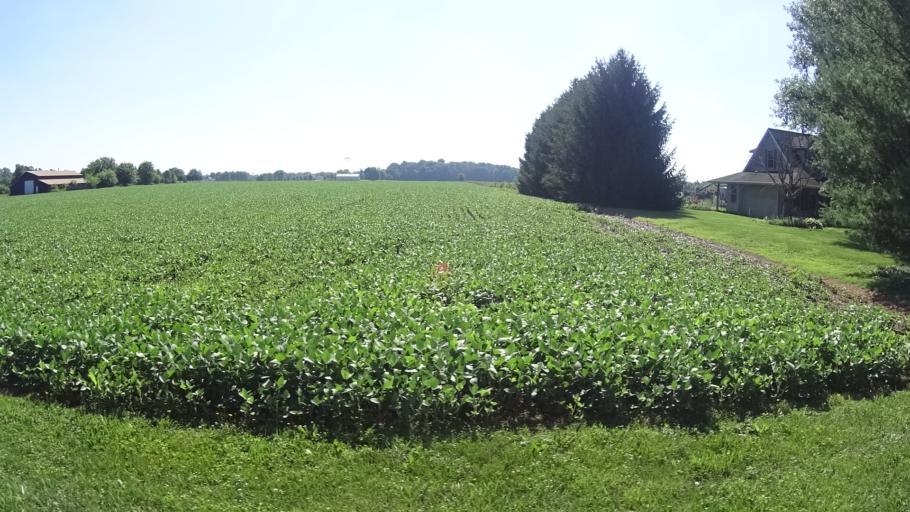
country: US
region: Indiana
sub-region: Madison County
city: Ingalls
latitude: 39.9725
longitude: -85.8150
